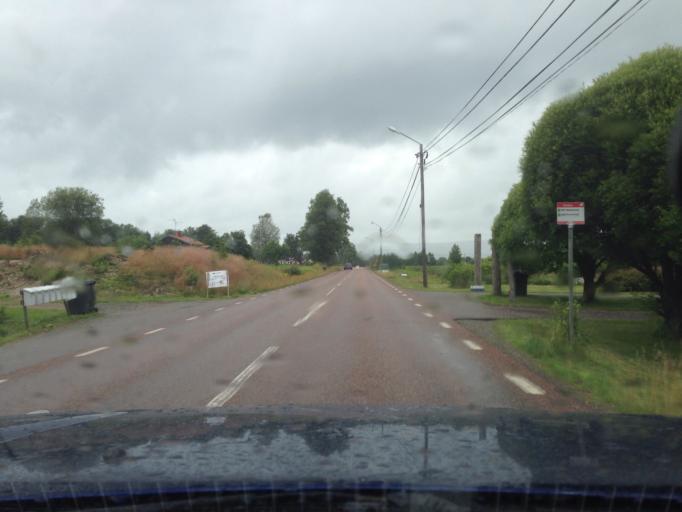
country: SE
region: Dalarna
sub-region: Ludvika Kommun
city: Grangesberg
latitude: 60.1390
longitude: 15.0000
